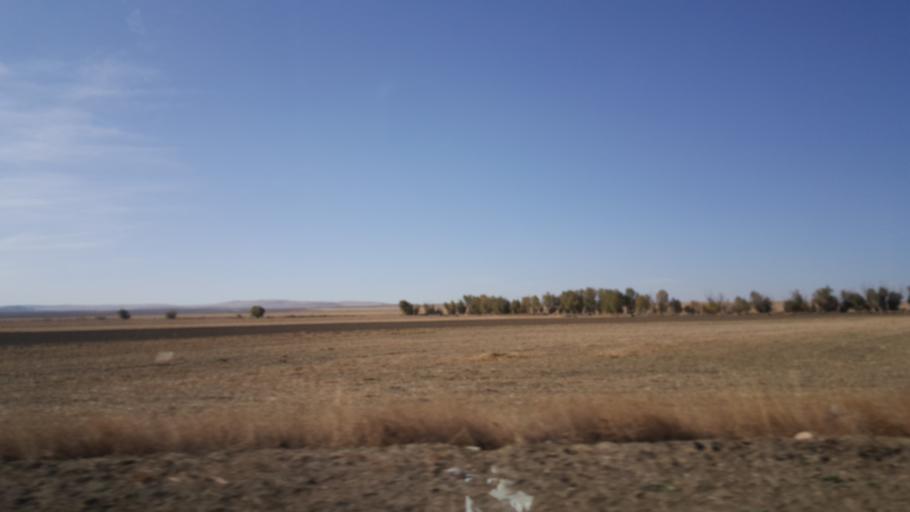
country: TR
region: Ankara
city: Yenice
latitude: 39.3751
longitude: 32.8146
